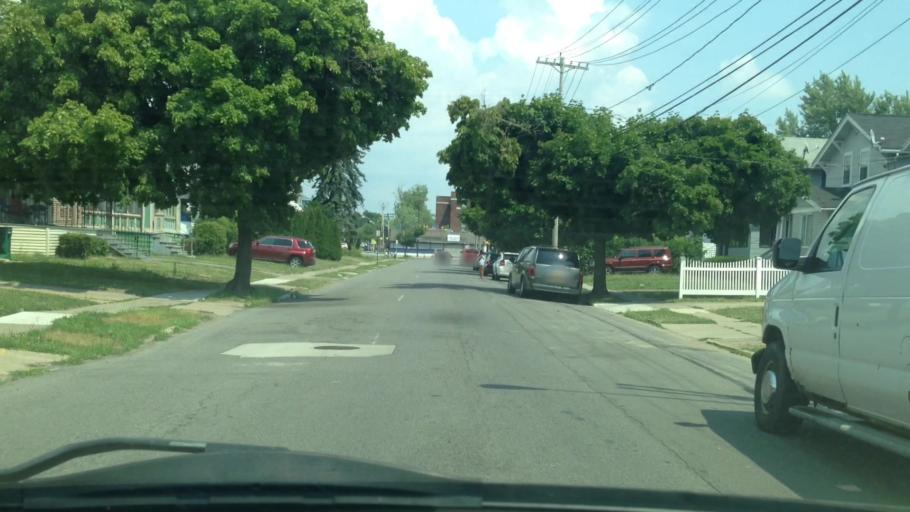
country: US
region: New York
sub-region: Erie County
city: Eggertsville
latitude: 42.9402
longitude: -78.8159
